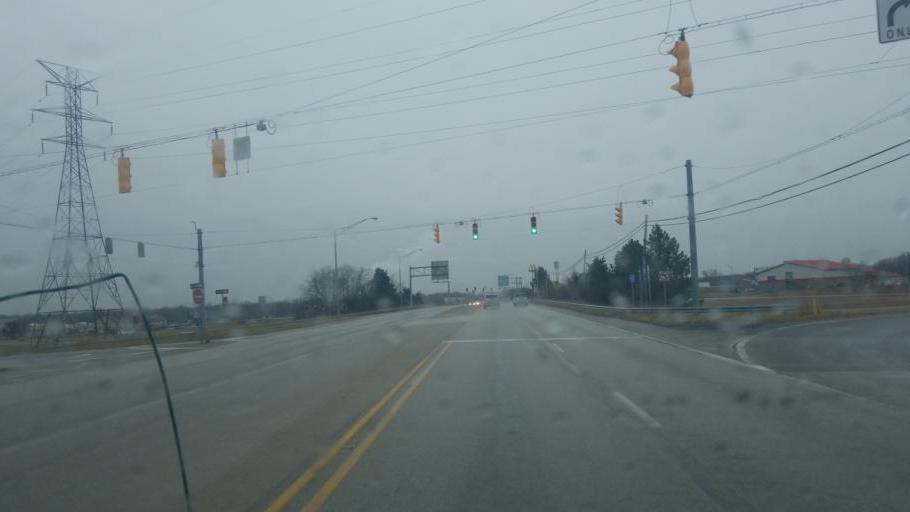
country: US
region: Indiana
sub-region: Shelby County
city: Shelbyville
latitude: 39.5529
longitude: -85.7758
